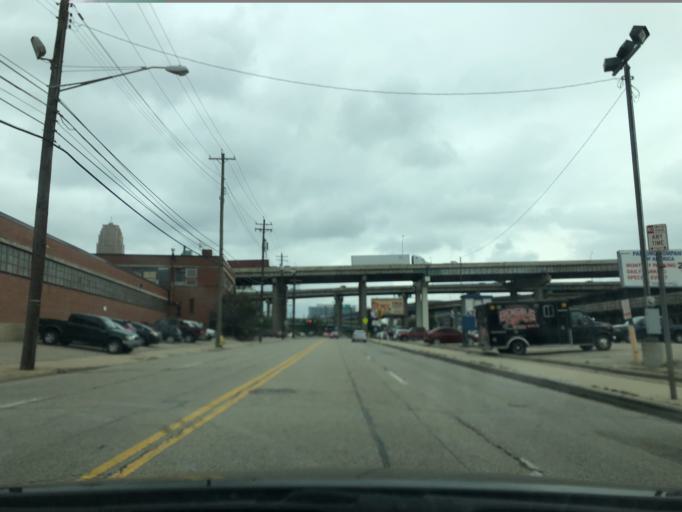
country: US
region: Kentucky
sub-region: Kenton County
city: Covington
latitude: 39.0972
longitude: -84.5241
